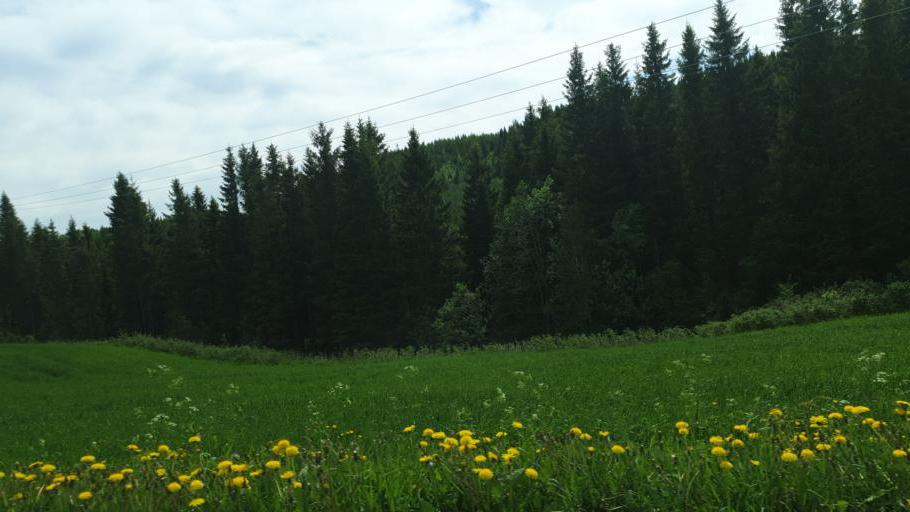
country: NO
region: Nord-Trondelag
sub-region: Leksvik
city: Leksvik
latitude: 63.6866
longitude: 10.5459
